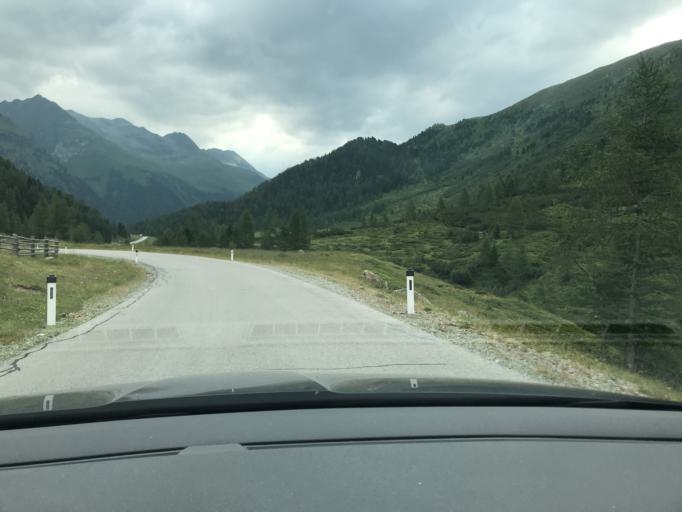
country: IT
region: Trentino-Alto Adige
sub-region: Bolzano
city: San Martino
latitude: 46.9021
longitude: 12.2267
